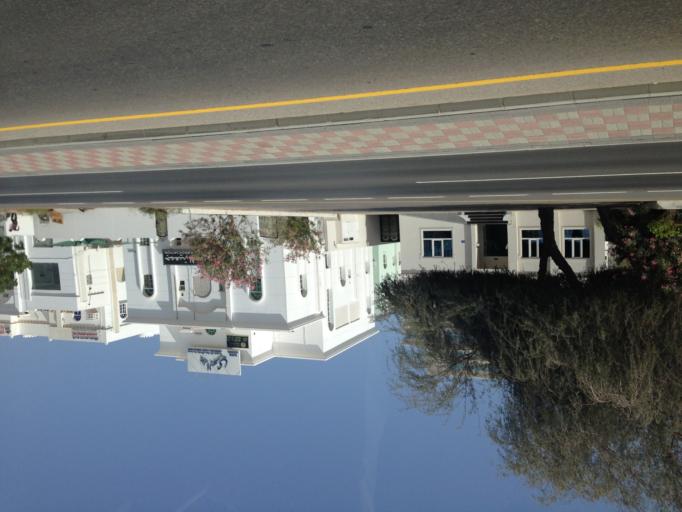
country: OM
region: Muhafazat Masqat
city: Bawshar
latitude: 23.6021
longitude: 58.3701
